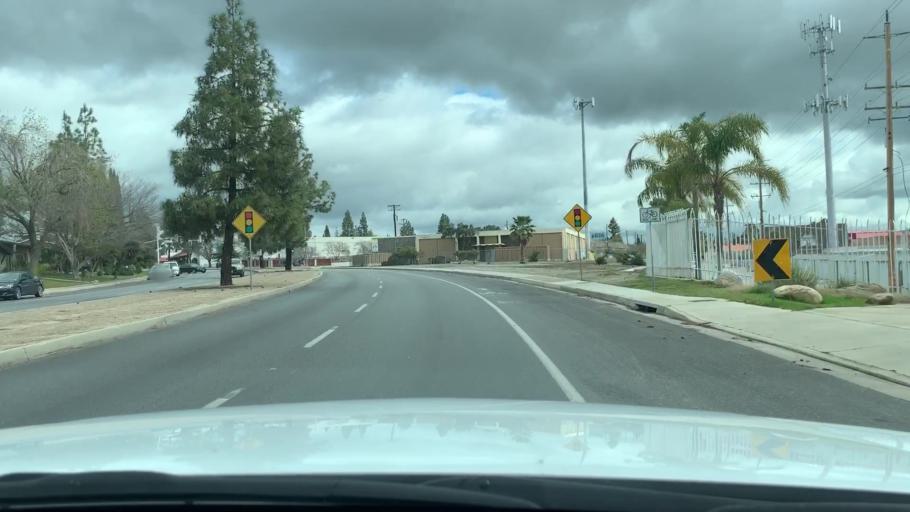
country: US
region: California
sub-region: Kern County
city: Oildale
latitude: 35.3977
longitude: -118.9548
